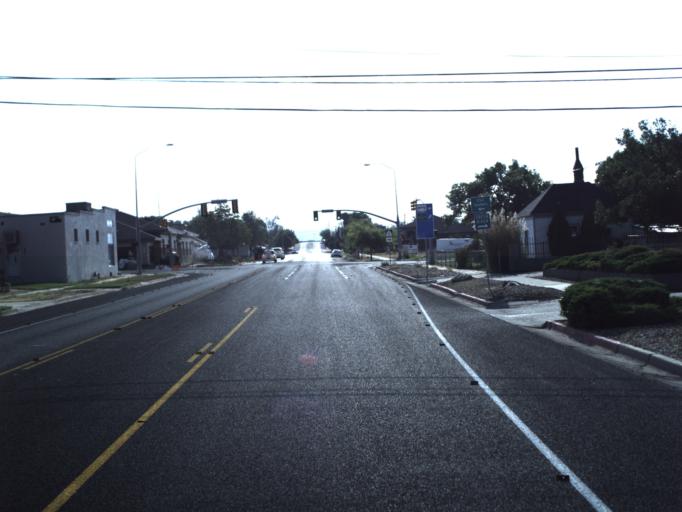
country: US
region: Utah
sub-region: Carbon County
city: Price
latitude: 39.6010
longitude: -110.8067
